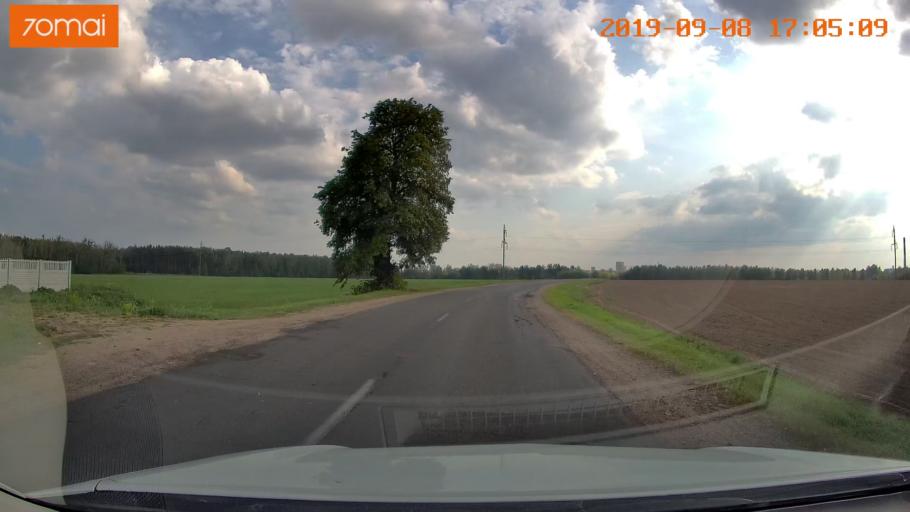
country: BY
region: Grodnenskaya
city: Hrodna
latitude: 53.6814
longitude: 23.9560
